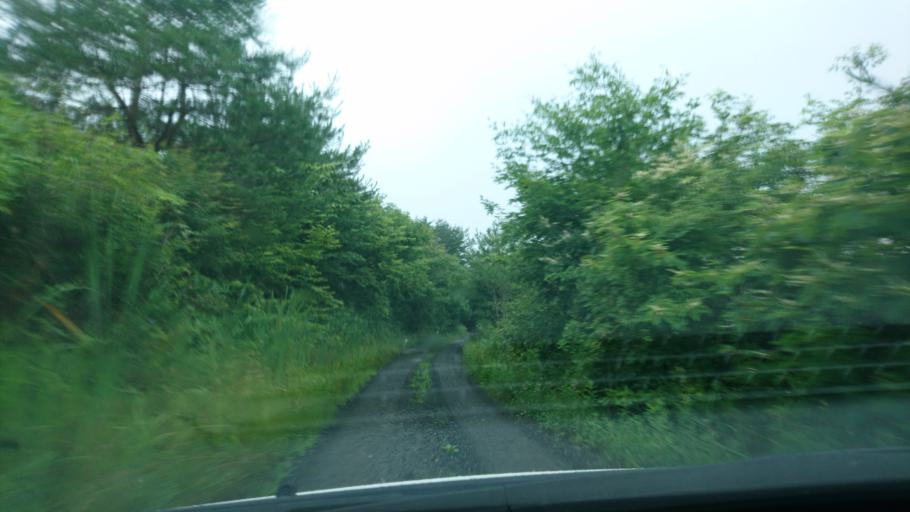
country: JP
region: Iwate
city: Ichinoseki
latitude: 38.9194
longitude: 141.1863
